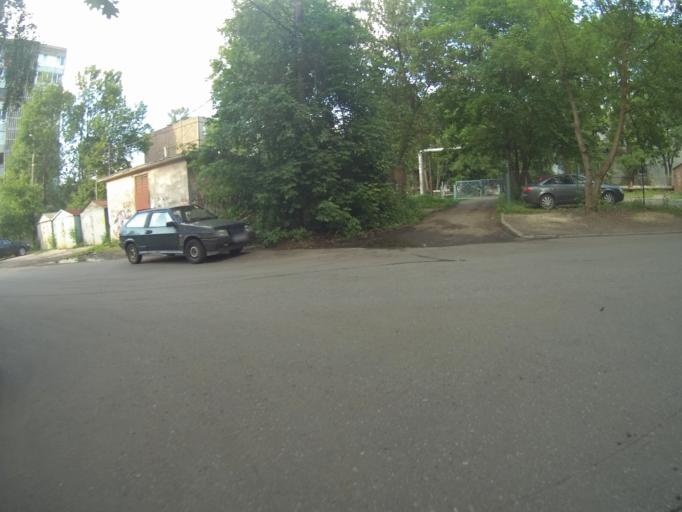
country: RU
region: Vladimir
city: Kommunar
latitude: 56.1724
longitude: 40.4624
